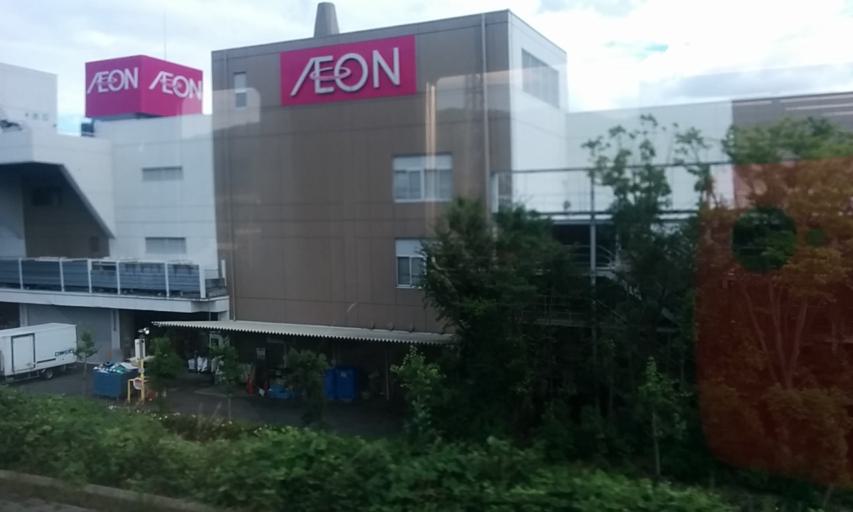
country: JP
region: Osaka
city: Takatsuki
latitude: 34.8596
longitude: 135.6434
